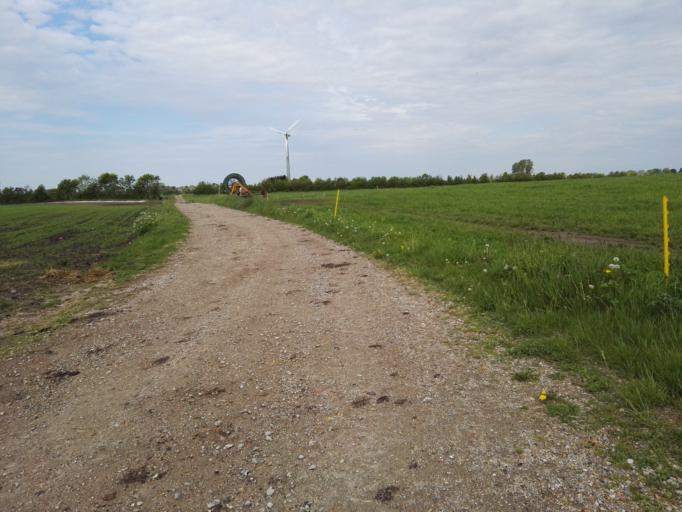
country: DK
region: Capital Region
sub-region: Frederikssund Kommune
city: Skibby
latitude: 55.7867
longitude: 11.9311
